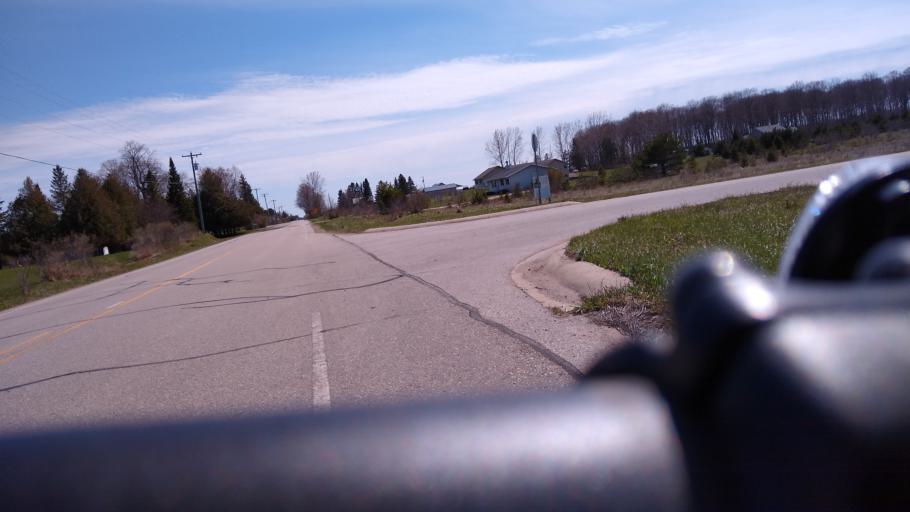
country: US
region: Michigan
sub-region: Delta County
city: Escanaba
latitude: 45.7195
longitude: -87.2025
